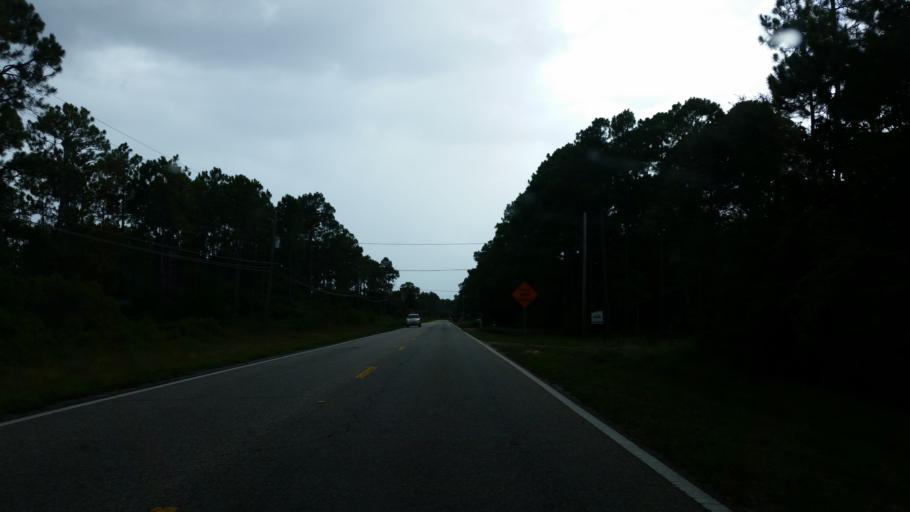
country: US
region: Florida
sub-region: Santa Rosa County
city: Woodlawn Beach
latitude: 30.4237
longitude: -86.9723
